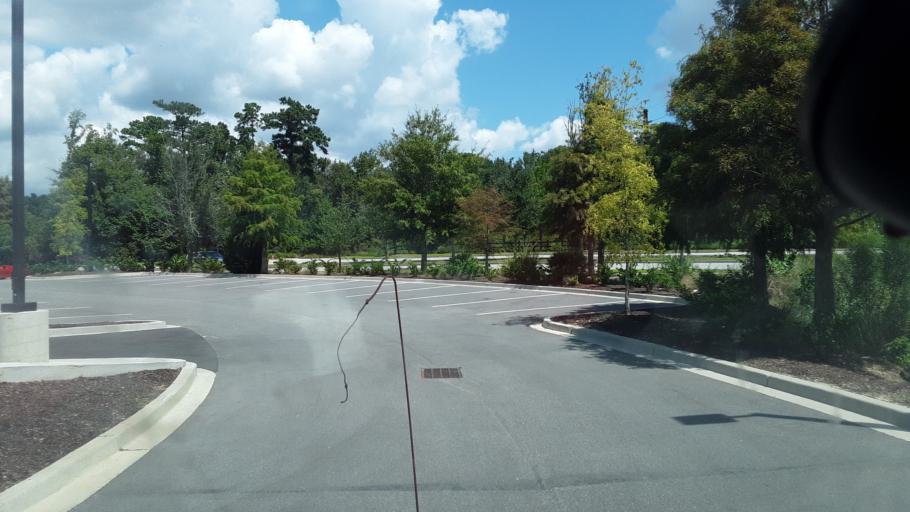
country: US
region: South Carolina
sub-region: Berkeley County
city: Sangaree
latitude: 33.0409
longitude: -80.1397
